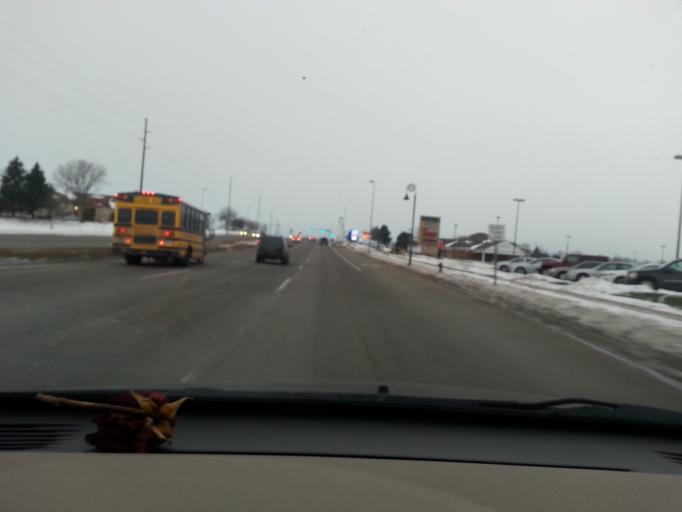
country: US
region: Minnesota
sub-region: Dakota County
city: Burnsville
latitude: 44.7467
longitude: -93.2944
